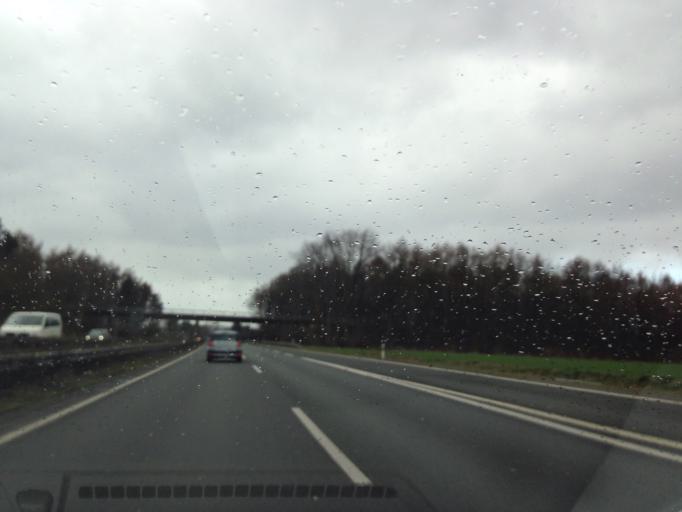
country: DE
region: North Rhine-Westphalia
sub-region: Regierungsbezirk Munster
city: Recklinghausen
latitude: 51.6562
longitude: 7.1659
